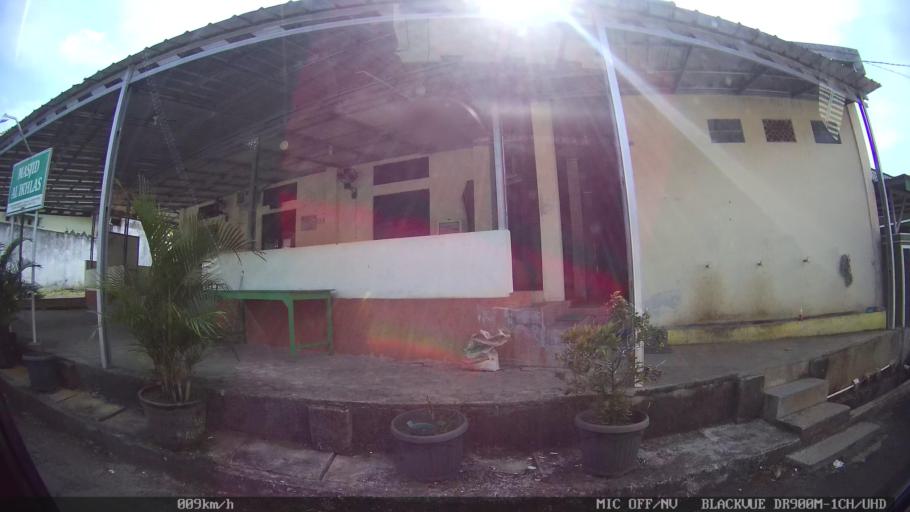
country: ID
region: Lampung
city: Kedaton
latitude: -5.3850
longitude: 105.2357
